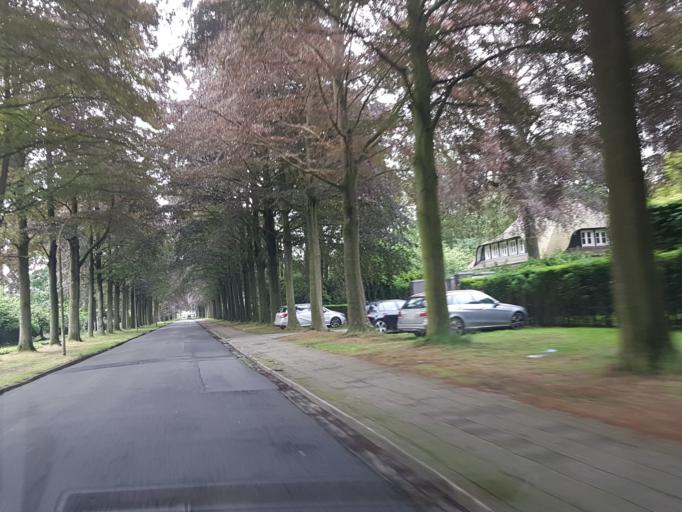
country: BE
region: Flanders
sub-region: Provincie Antwerpen
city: Brasschaat
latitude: 51.2861
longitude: 4.4734
